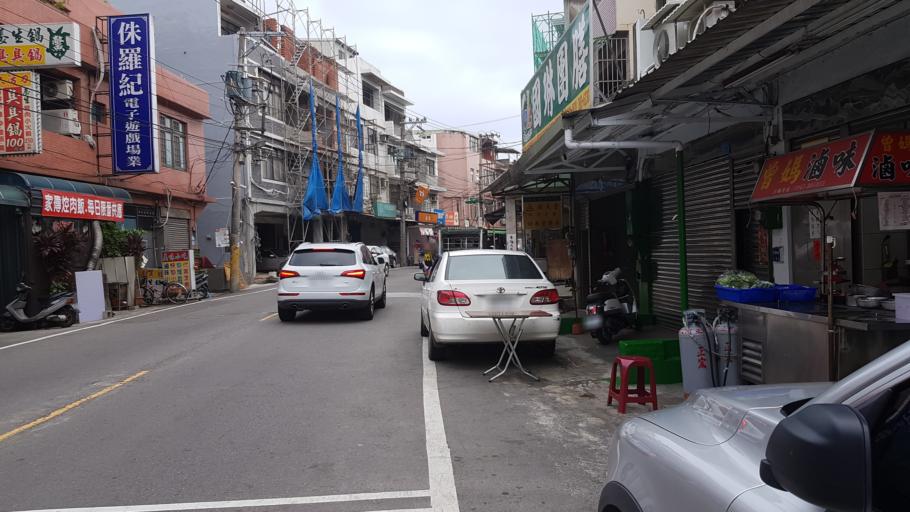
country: TW
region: Taiwan
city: Taoyuan City
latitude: 25.0786
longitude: 121.2574
